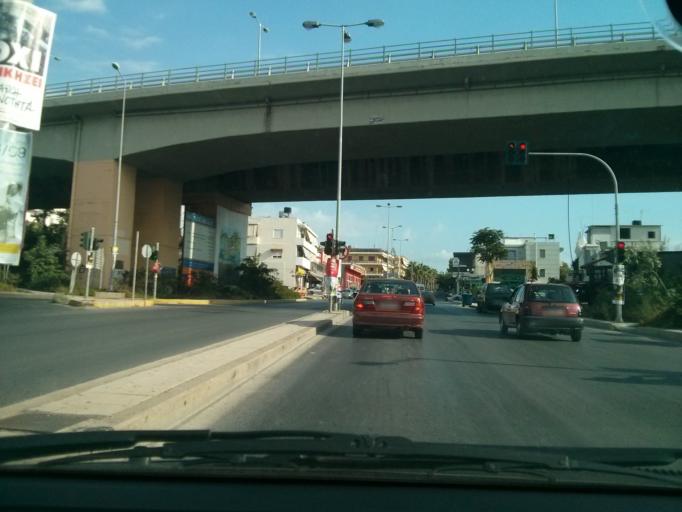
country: GR
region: Crete
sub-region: Nomos Irakleiou
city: Irakleion
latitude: 35.3210
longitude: 25.1433
